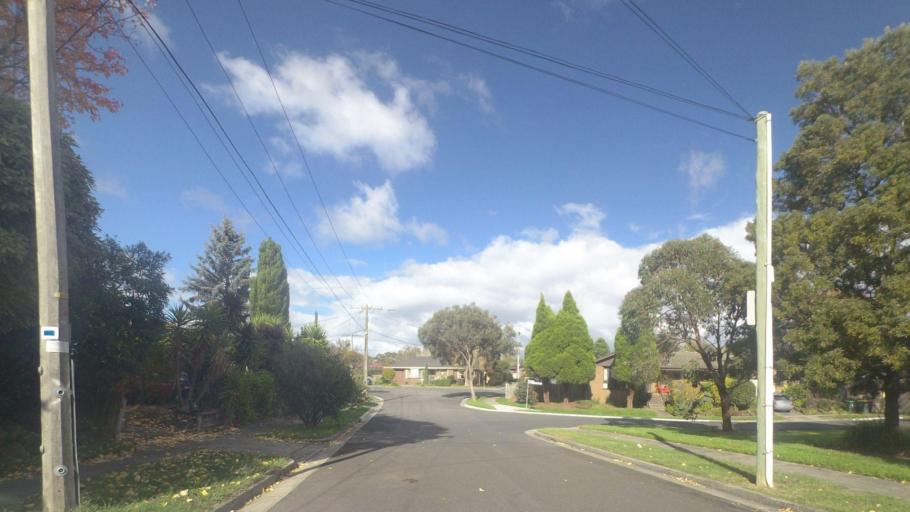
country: AU
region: Victoria
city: Forest Hill
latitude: -37.8378
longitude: 145.1794
